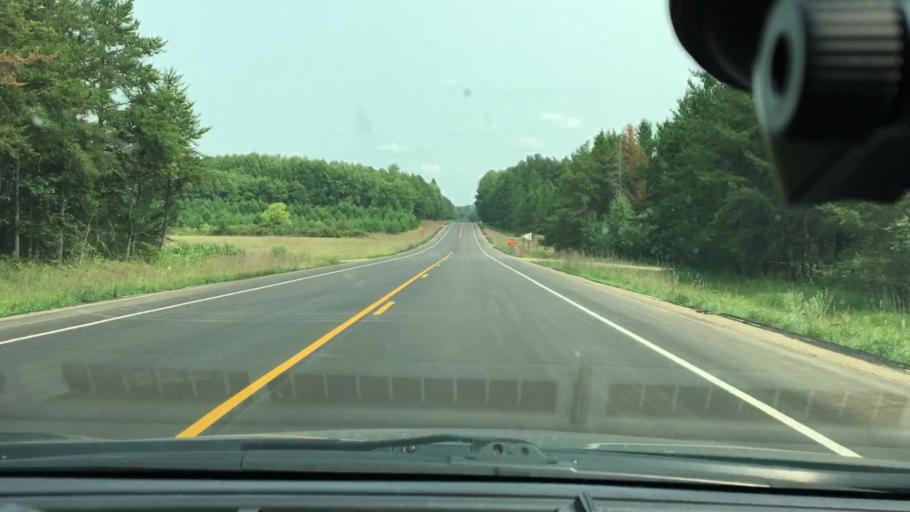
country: US
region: Minnesota
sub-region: Crow Wing County
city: Nisswa
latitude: 46.5295
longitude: -94.2432
